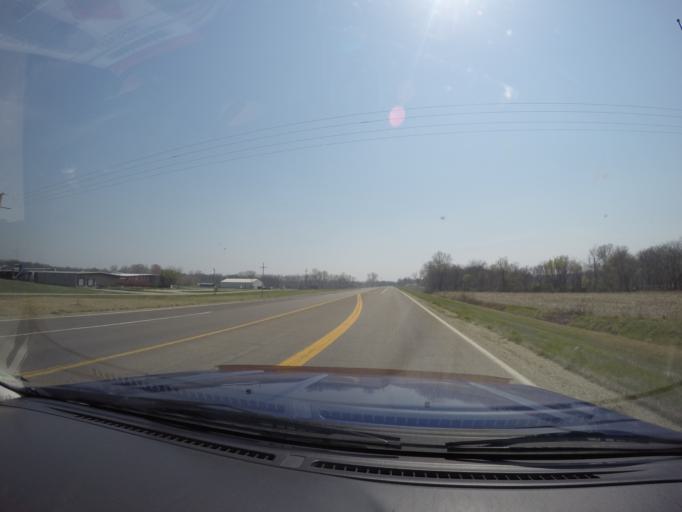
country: US
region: Kansas
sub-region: Morris County
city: Council Grove
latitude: 38.6739
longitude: -96.4885
